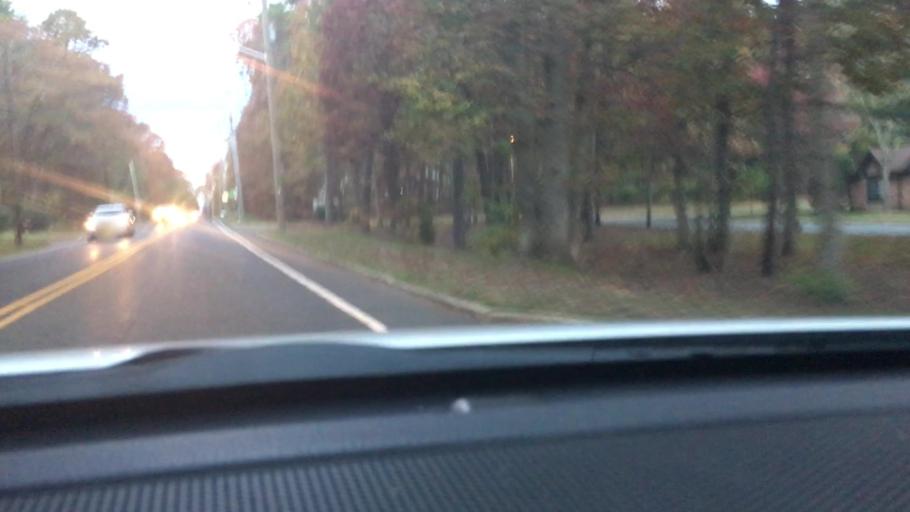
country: US
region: New Jersey
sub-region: Atlantic County
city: Absecon
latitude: 39.4431
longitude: -74.4974
